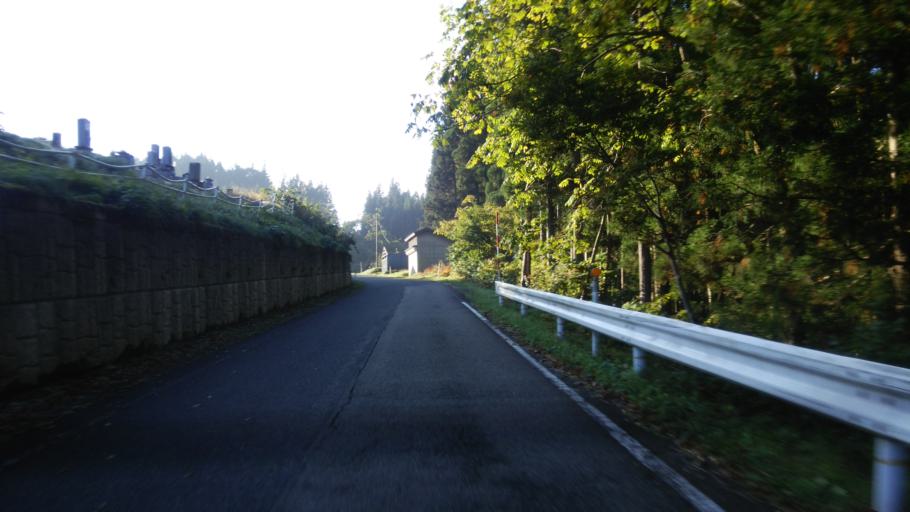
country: JP
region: Fukushima
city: Kitakata
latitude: 37.4231
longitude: 139.7248
